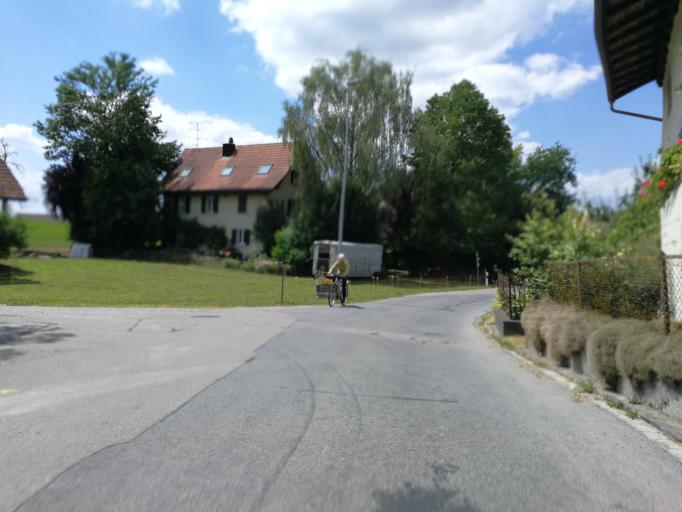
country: CH
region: Zurich
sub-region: Bezirk Hinwil
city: Gruet
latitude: 47.2891
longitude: 8.7805
